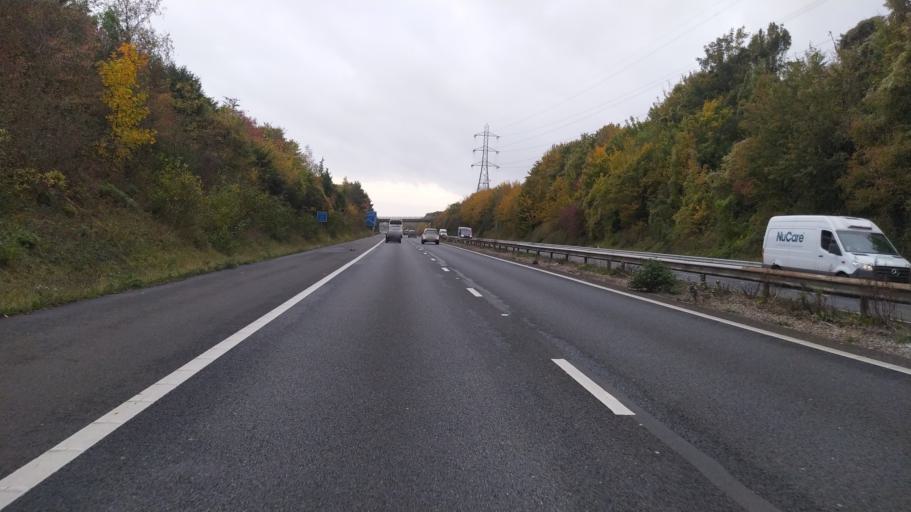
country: GB
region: England
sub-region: Hampshire
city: Cowplain
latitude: 50.9160
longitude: -0.9987
